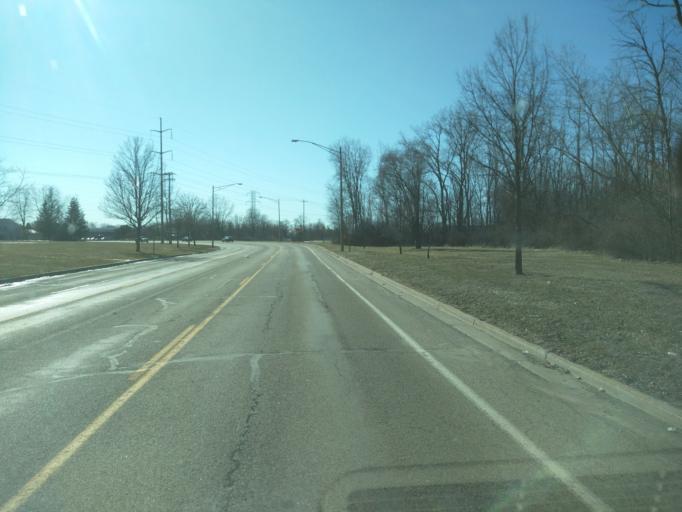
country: US
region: Michigan
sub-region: Ingham County
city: Lansing
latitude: 42.6777
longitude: -84.5851
